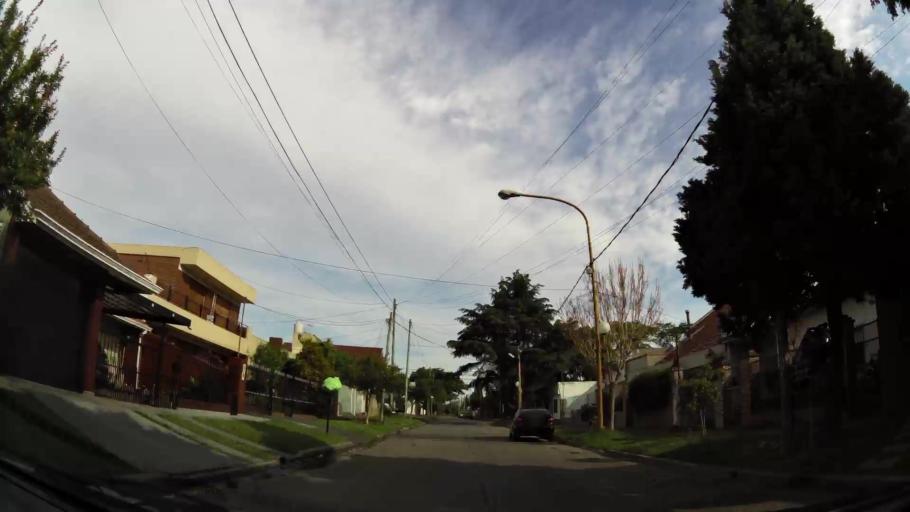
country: AR
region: Buenos Aires
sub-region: Partido de Quilmes
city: Quilmes
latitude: -34.7567
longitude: -58.2863
